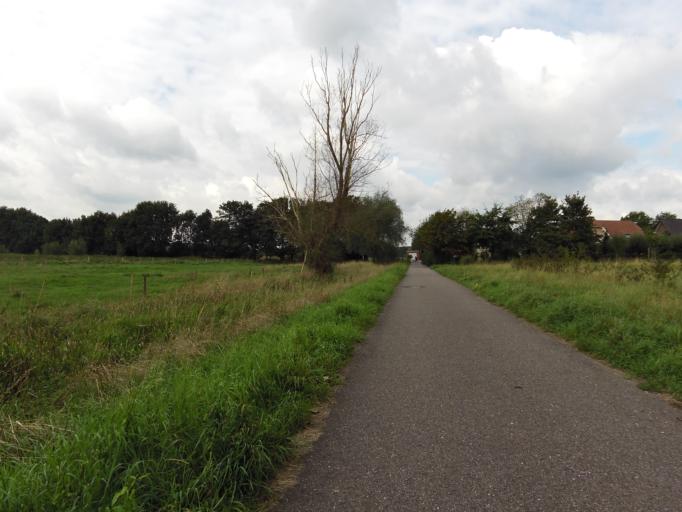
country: DE
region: North Rhine-Westphalia
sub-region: Regierungsbezirk Koln
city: Gangelt
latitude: 50.9846
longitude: 6.0354
